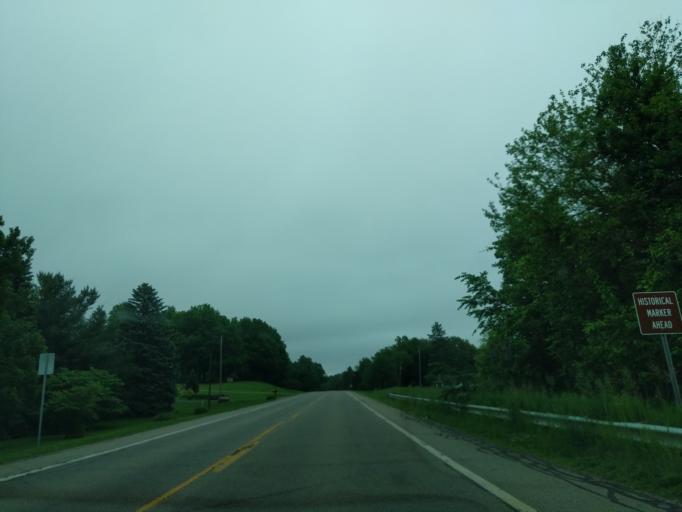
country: US
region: Michigan
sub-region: Hillsdale County
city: Litchfield
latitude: 42.0352
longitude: -84.7360
